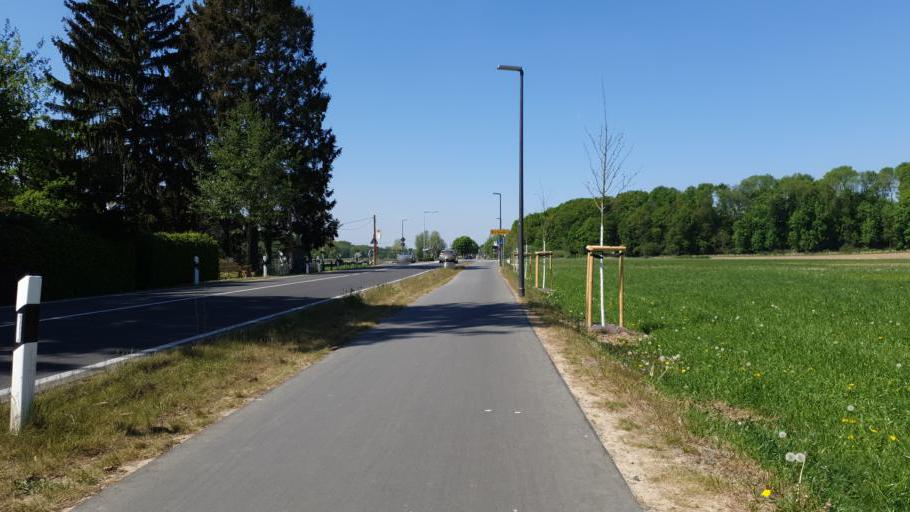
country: DE
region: North Rhine-Westphalia
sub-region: Regierungsbezirk Koln
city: Odenthal
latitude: 51.0275
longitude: 7.0761
